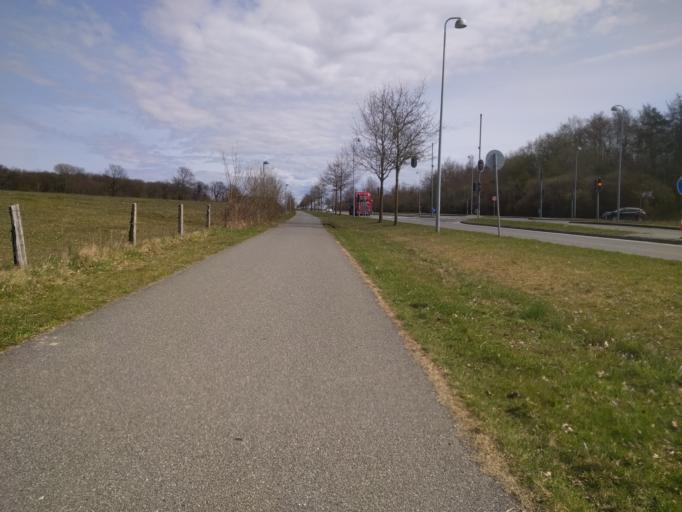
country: DK
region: South Denmark
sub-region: Odense Kommune
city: Neder Holluf
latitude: 55.3752
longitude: 10.4674
